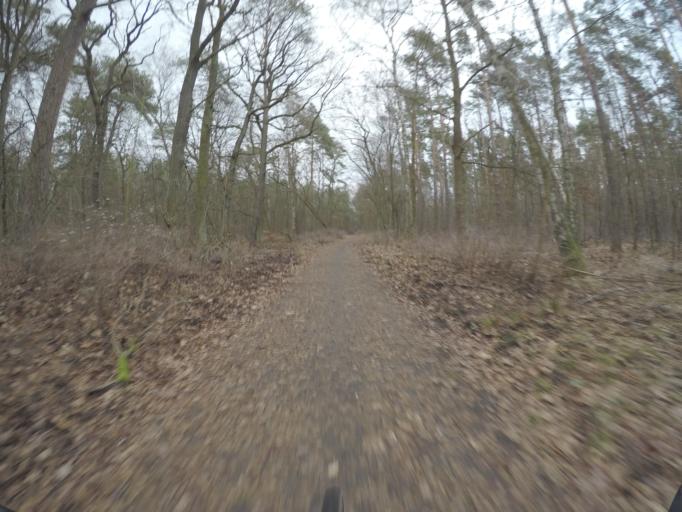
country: DE
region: Berlin
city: Grunau
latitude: 52.4204
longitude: 13.6035
